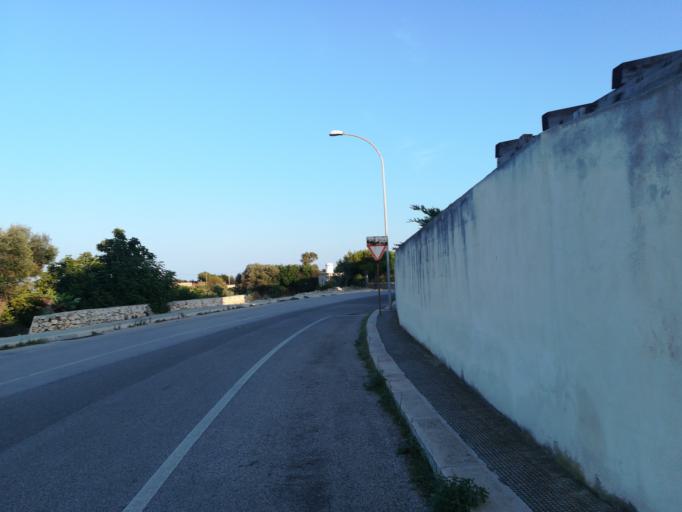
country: IT
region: Apulia
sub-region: Provincia di Bari
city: Polignano a Mare
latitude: 40.9909
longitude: 17.2317
